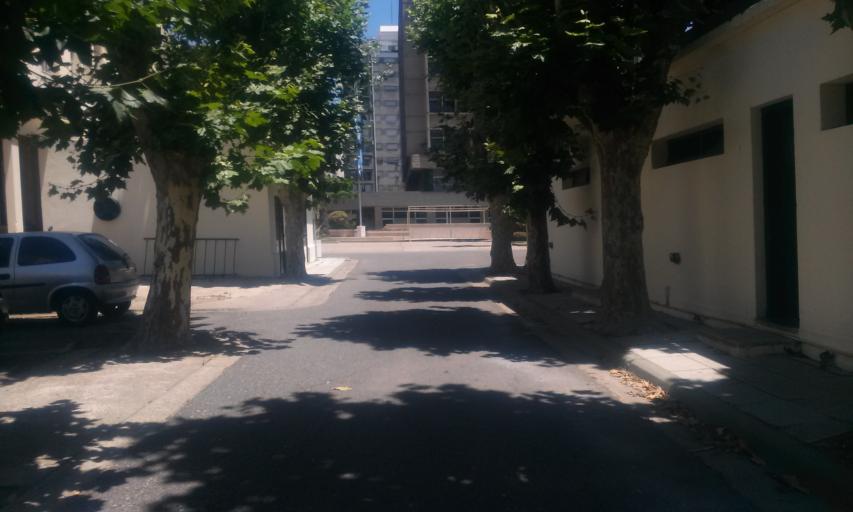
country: AR
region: Buenos Aires F.D.
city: Colegiales
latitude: -34.5713
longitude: -58.4397
